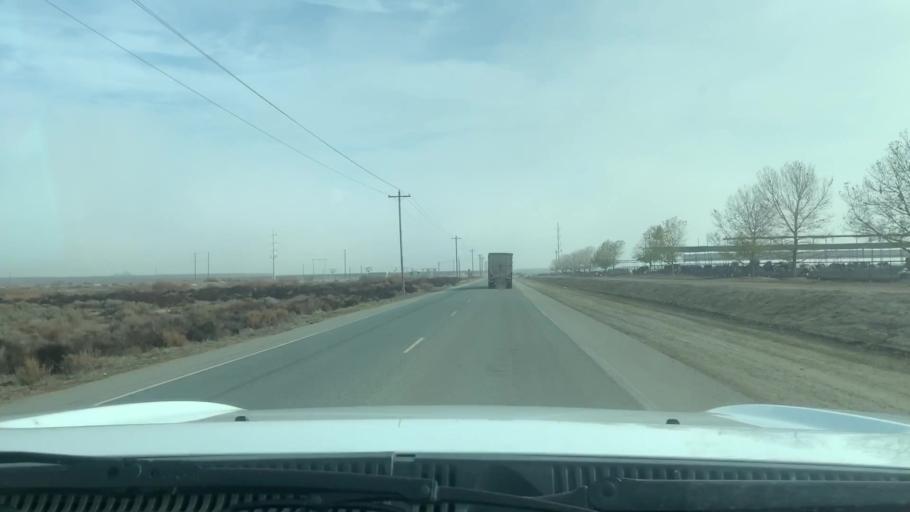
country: US
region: California
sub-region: Kern County
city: Buttonwillow
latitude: 35.5005
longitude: -119.4536
